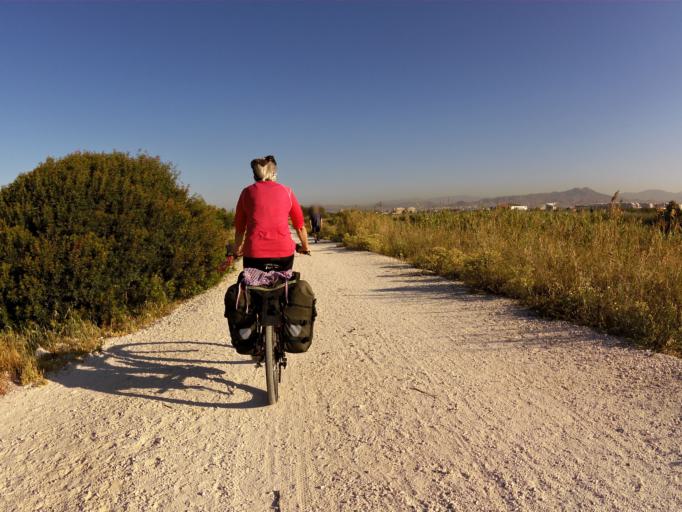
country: ES
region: Andalusia
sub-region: Provincia de Malaga
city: Torremolinos
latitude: 36.6680
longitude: -4.4580
